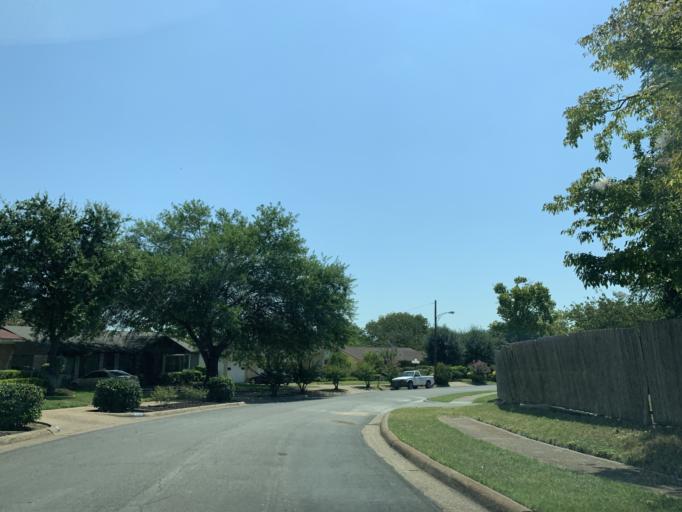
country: US
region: Texas
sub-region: Dallas County
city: Hutchins
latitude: 32.6757
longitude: -96.7526
